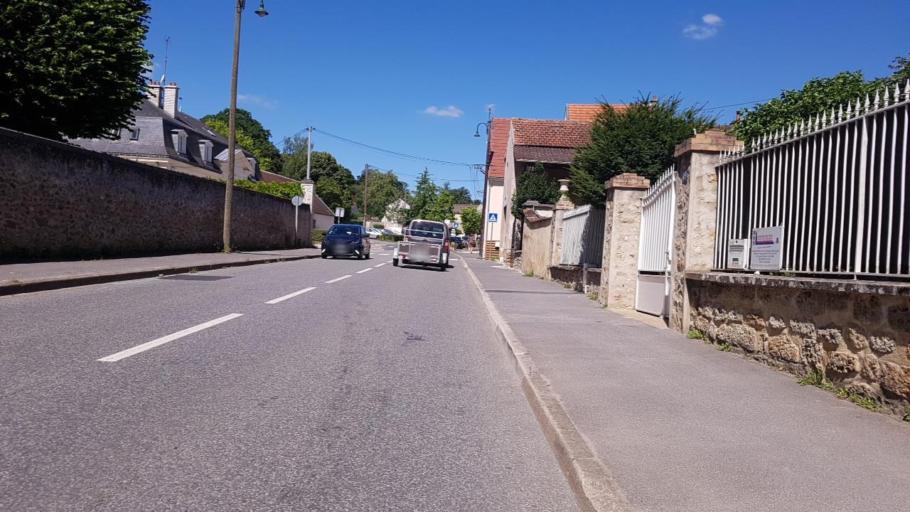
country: FR
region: Ile-de-France
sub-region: Departement de Seine-et-Marne
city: Saacy-sur-Marne
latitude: 48.9718
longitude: 3.1880
